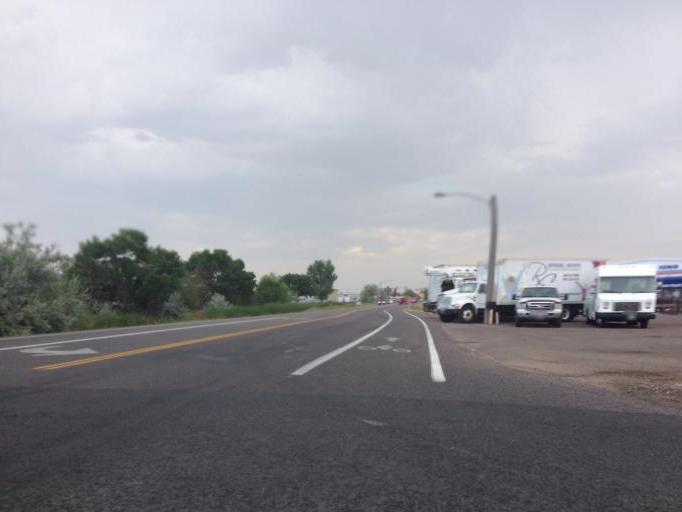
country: US
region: Colorado
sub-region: Larimer County
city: Fort Collins
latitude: 40.5877
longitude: -105.0529
